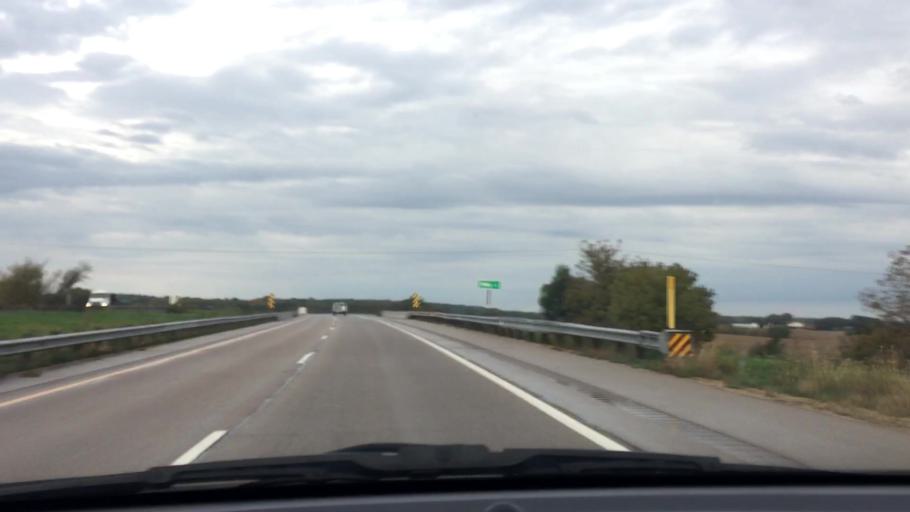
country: US
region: Wisconsin
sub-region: Rock County
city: Clinton
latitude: 42.5734
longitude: -88.8879
